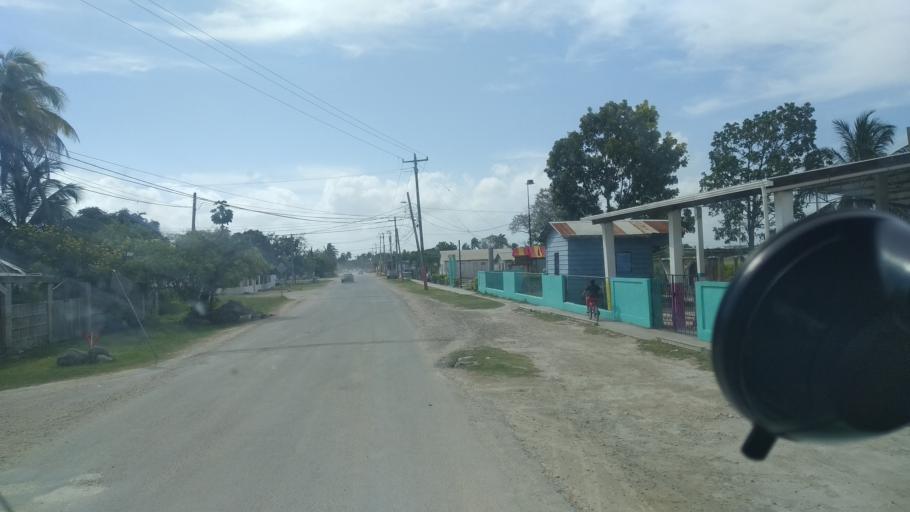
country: BZ
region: Corozal
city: Corozal
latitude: 18.4022
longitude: -88.3832
